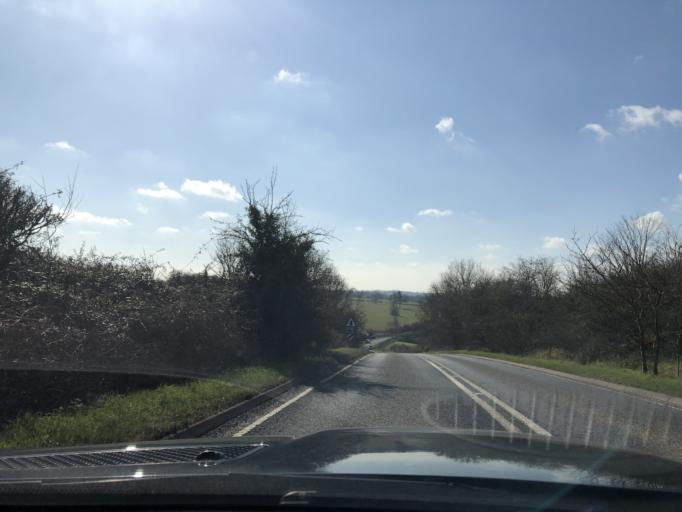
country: GB
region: England
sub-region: Warwickshire
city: Ryton on Dunsmore
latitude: 52.3289
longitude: -1.4161
